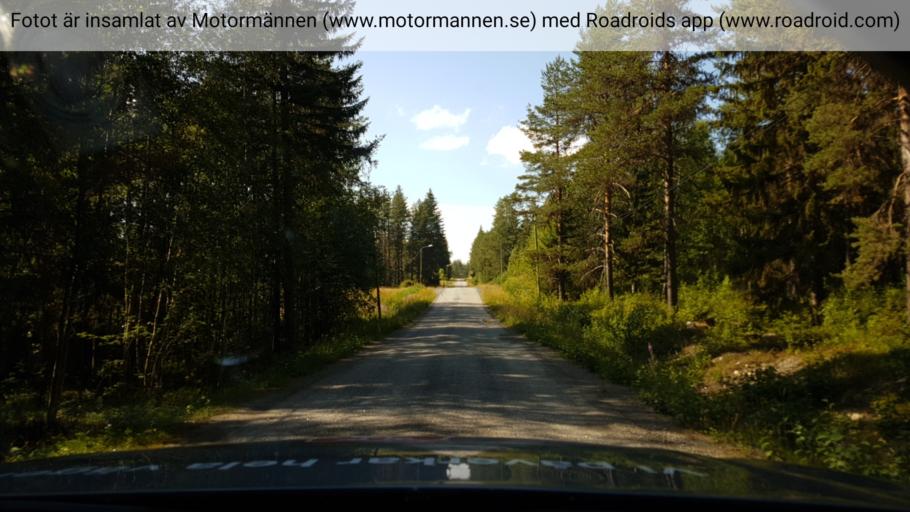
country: SE
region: Vaesterbotten
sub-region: Dorotea Kommun
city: Dorotea
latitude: 64.0995
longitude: 16.4081
